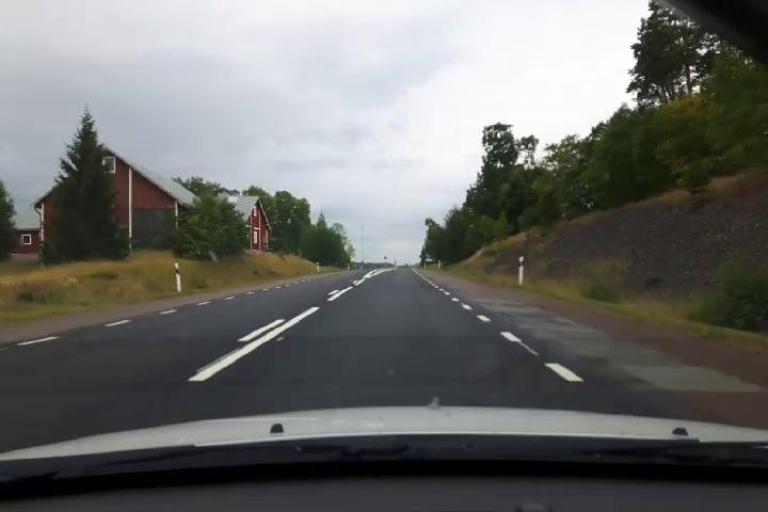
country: SE
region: Uppsala
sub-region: Uppsala Kommun
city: Gamla Uppsala
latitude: 59.9015
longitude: 17.6117
